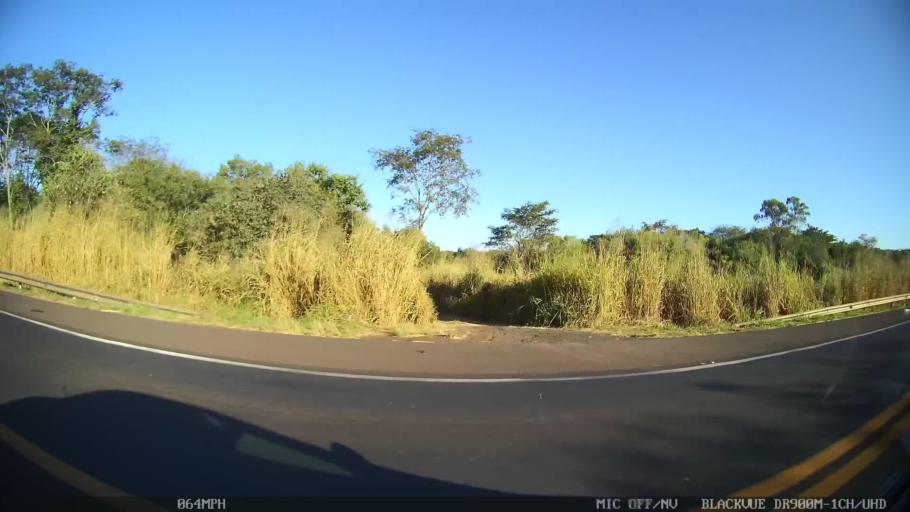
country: BR
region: Sao Paulo
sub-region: Guapiacu
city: Guapiacu
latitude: -20.7437
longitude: -49.1078
